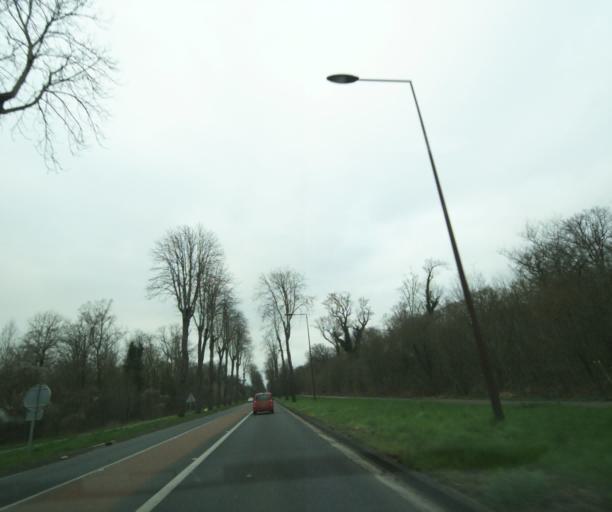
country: FR
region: Ile-de-France
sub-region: Departement des Yvelines
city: Poissy
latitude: 48.9165
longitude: 2.0649
